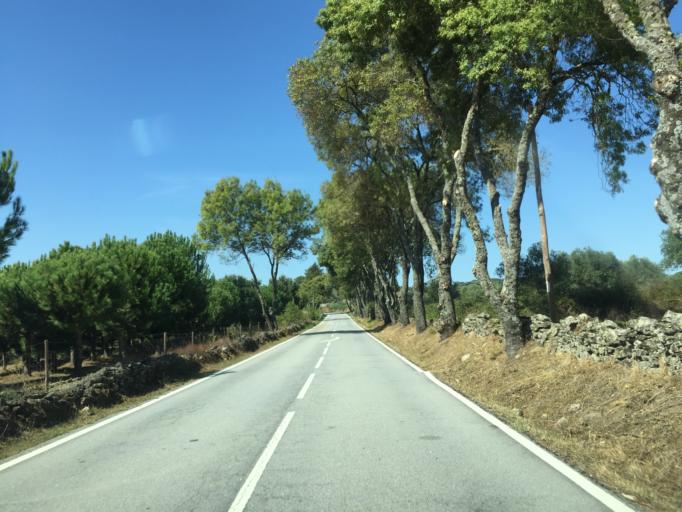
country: PT
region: Portalegre
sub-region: Portalegre
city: Alagoa
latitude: 39.4337
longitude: -7.5305
